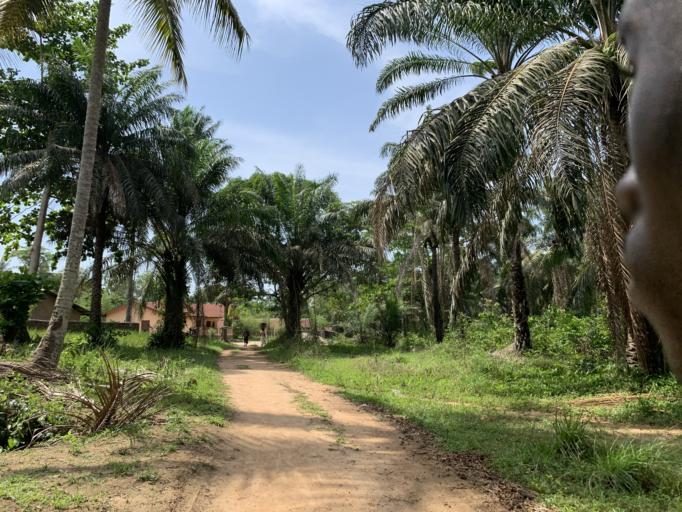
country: SL
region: Western Area
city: Waterloo
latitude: 8.3649
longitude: -13.0476
